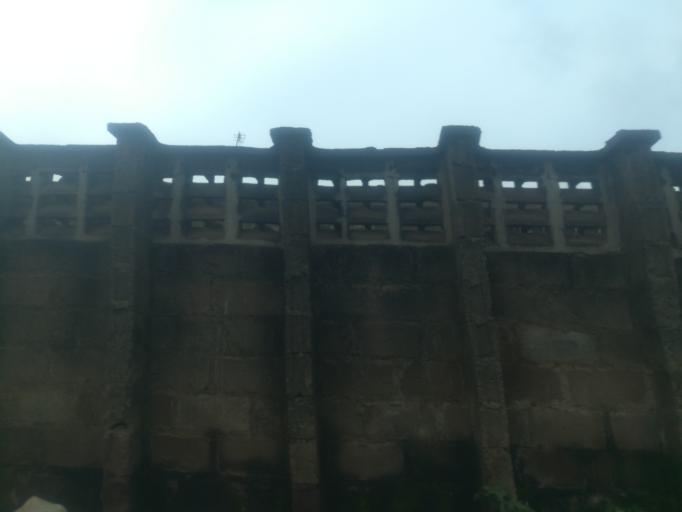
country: NG
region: Oyo
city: Ibadan
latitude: 7.3771
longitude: 3.9617
